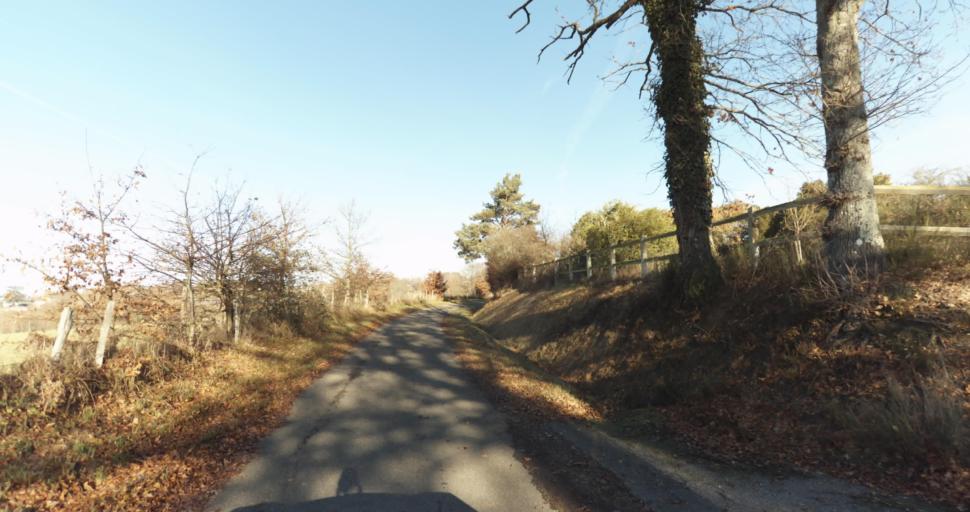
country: FR
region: Limousin
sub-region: Departement de la Haute-Vienne
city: Aixe-sur-Vienne
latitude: 45.8084
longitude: 1.1573
